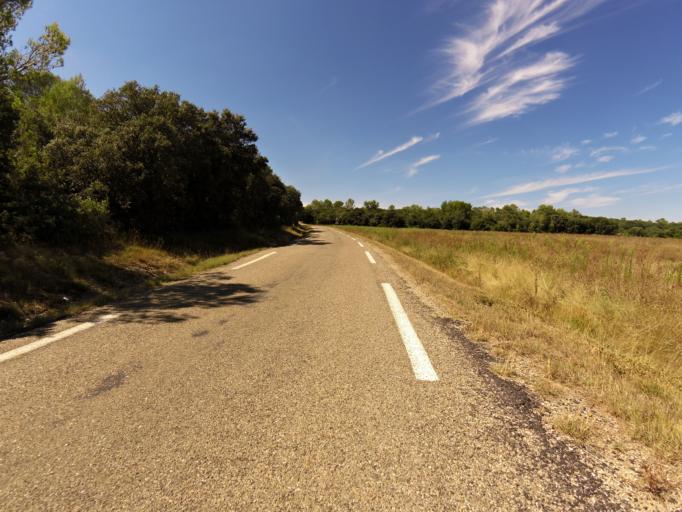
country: FR
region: Languedoc-Roussillon
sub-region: Departement du Gard
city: Sommieres
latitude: 43.8476
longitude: 4.0521
